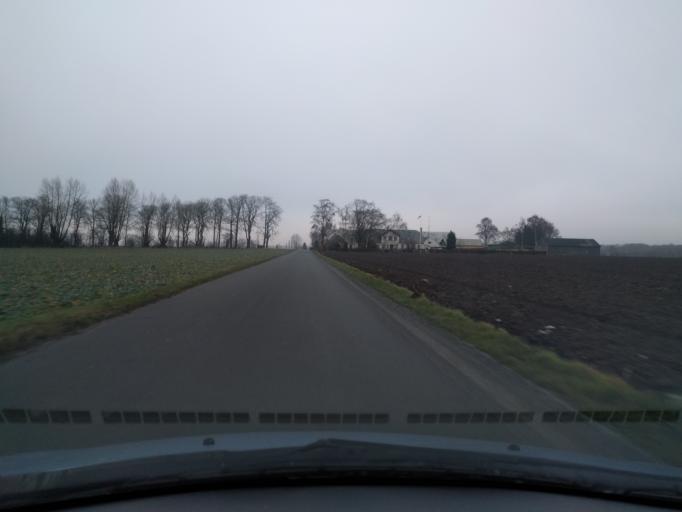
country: DK
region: South Denmark
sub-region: Odense Kommune
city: Bullerup
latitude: 55.4103
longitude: 10.5142
